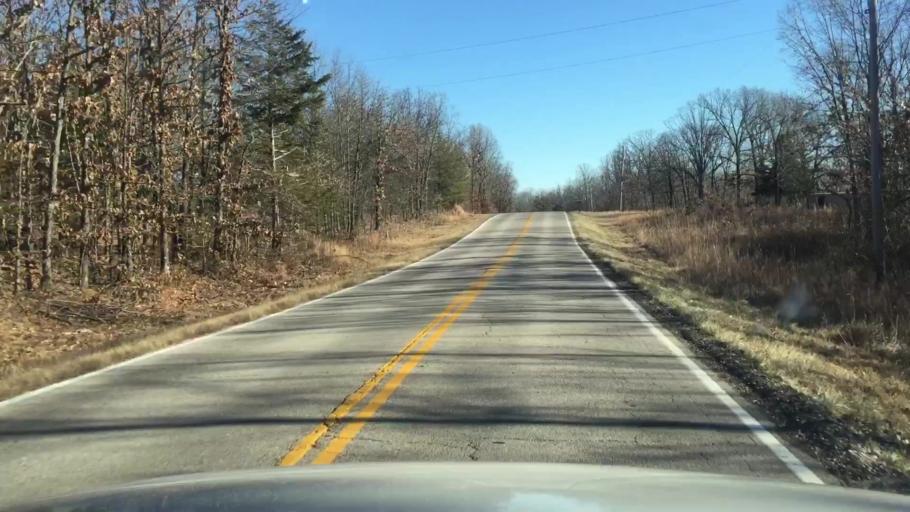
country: US
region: Missouri
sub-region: Morgan County
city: Versailles
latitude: 38.3471
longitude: -92.7423
